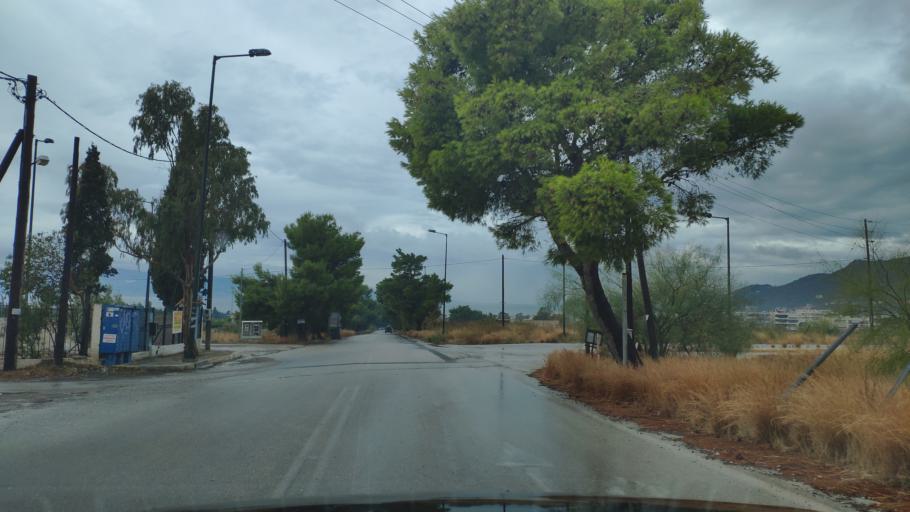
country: GR
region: Peloponnese
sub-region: Nomos Korinthias
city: Loutraki
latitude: 37.9660
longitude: 22.9875
